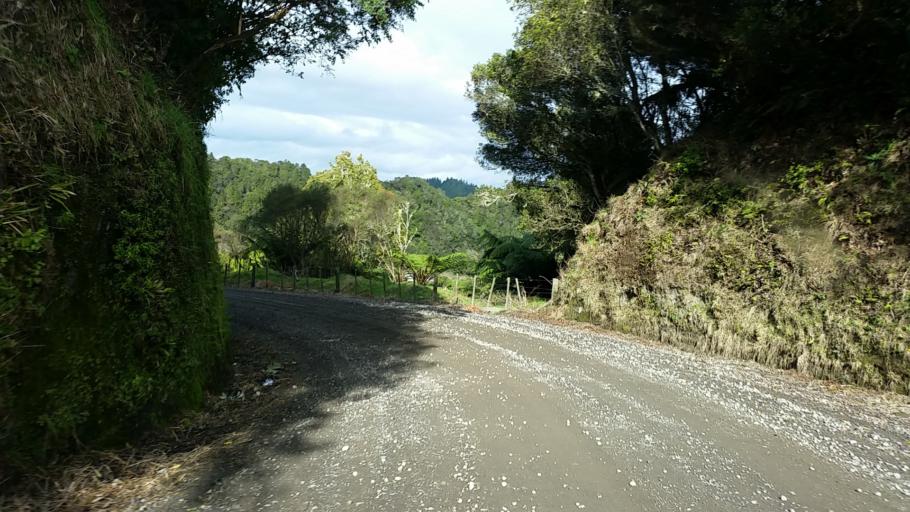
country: NZ
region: Taranaki
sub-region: South Taranaki District
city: Eltham
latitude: -39.1758
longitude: 174.6279
